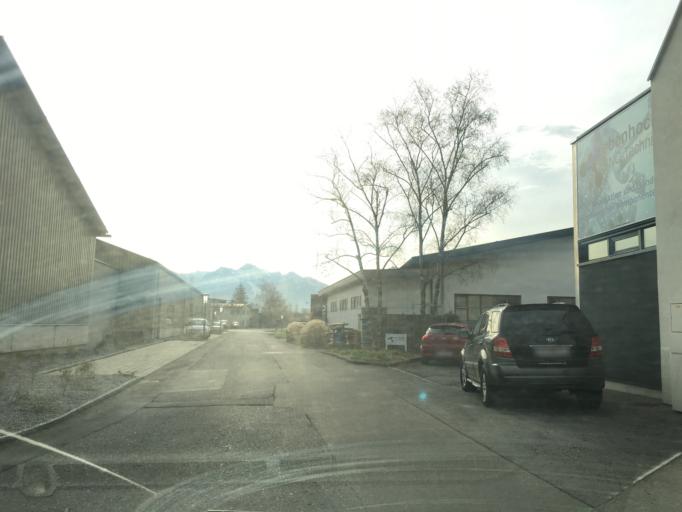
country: AT
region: Vorarlberg
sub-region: Politischer Bezirk Feldkirch
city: Klaus
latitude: 47.3090
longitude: 9.6341
